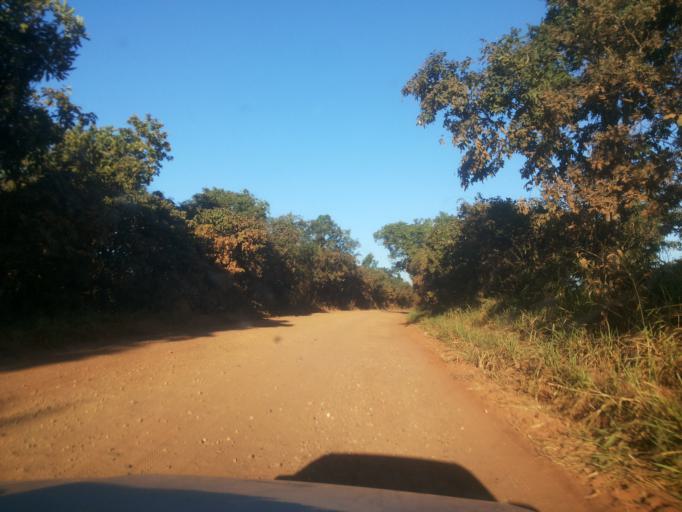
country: BR
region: Minas Gerais
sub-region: Campina Verde
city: Campina Verde
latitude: -19.3264
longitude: -49.7755
